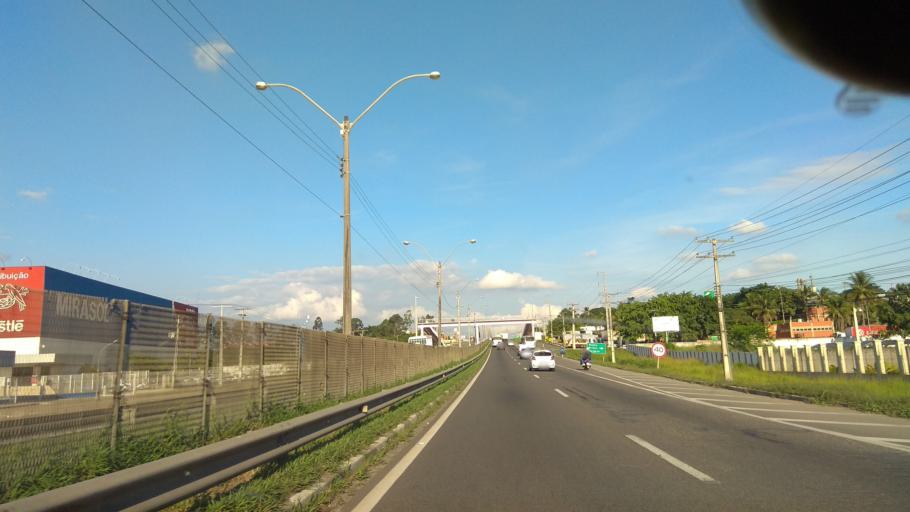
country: BR
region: Bahia
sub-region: Feira De Santana
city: Feira de Santana
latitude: -12.2891
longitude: -38.9133
